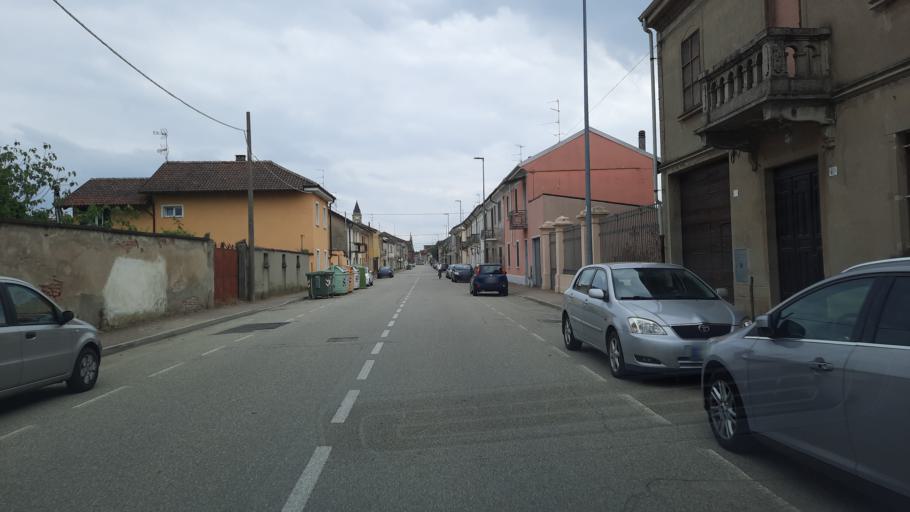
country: IT
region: Lombardy
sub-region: Provincia di Pavia
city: Palestro
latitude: 45.3049
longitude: 8.5336
